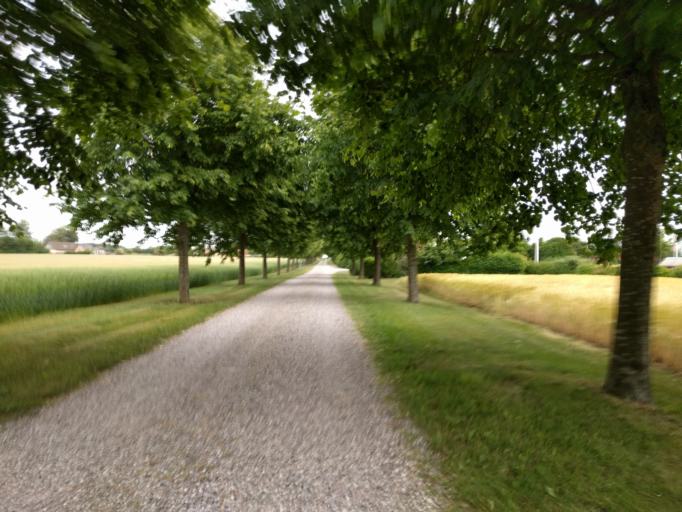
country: DK
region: South Denmark
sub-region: Kerteminde Kommune
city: Langeskov
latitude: 55.3943
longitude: 10.5890
